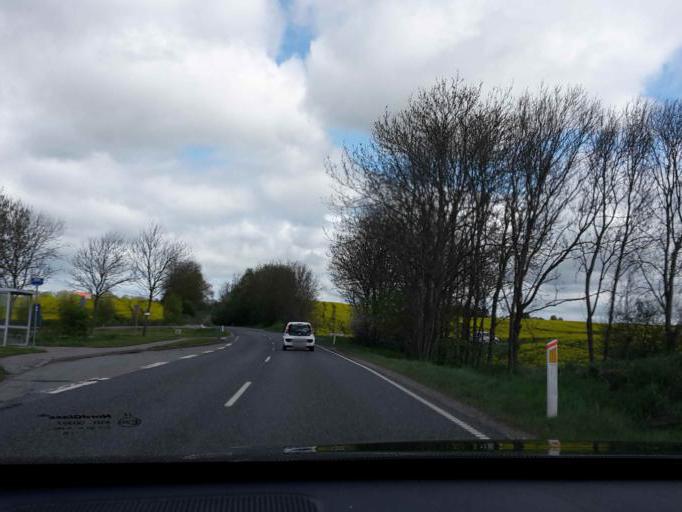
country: DK
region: Central Jutland
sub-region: Syddjurs Kommune
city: Hornslet
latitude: 56.3558
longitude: 10.3480
